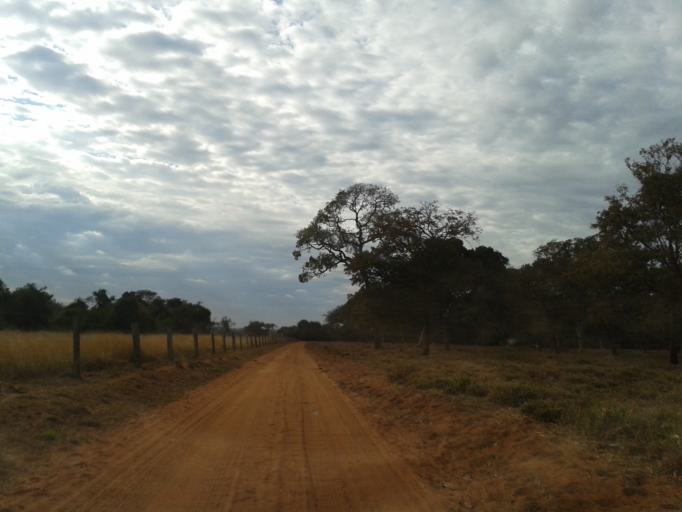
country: BR
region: Minas Gerais
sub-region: Santa Vitoria
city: Santa Vitoria
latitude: -18.7511
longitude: -50.1986
